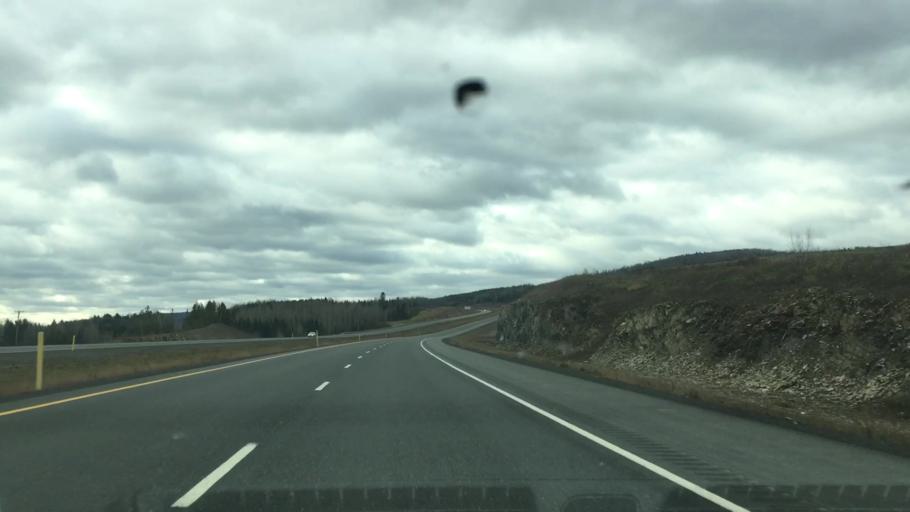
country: US
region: Maine
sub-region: Aroostook County
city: Fort Fairfield
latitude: 46.7354
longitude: -67.7188
